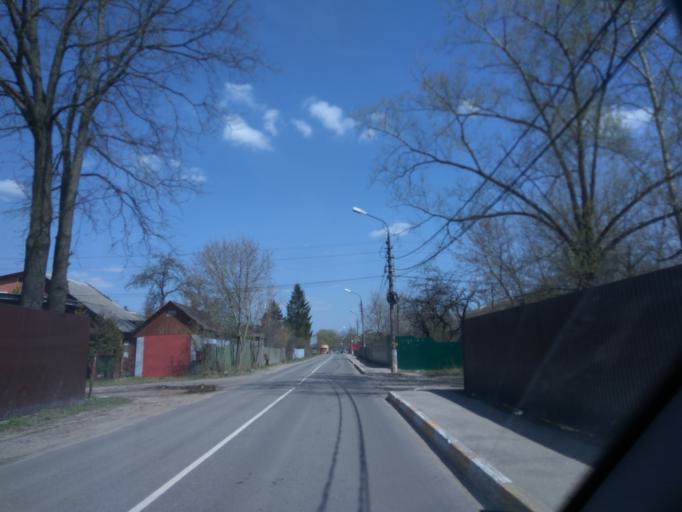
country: RU
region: Moskovskaya
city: Ramenskoye
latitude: 55.5609
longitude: 38.2160
